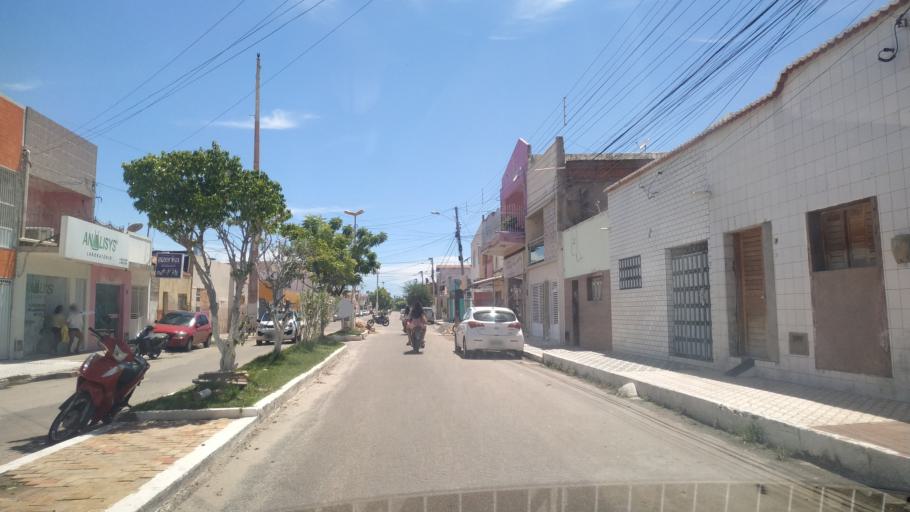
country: BR
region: Rio Grande do Norte
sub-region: Areia Branca
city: Areia Branca
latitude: -4.9567
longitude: -37.1319
